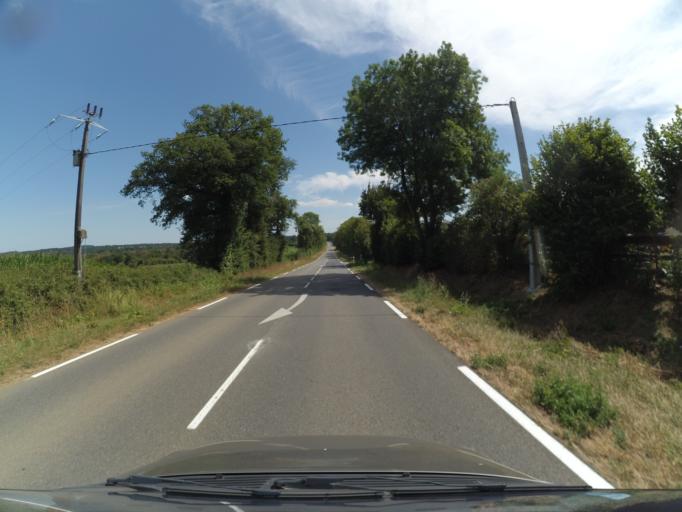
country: FR
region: Poitou-Charentes
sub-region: Departement de la Charente
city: Confolens
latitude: 45.9760
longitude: 0.6867
